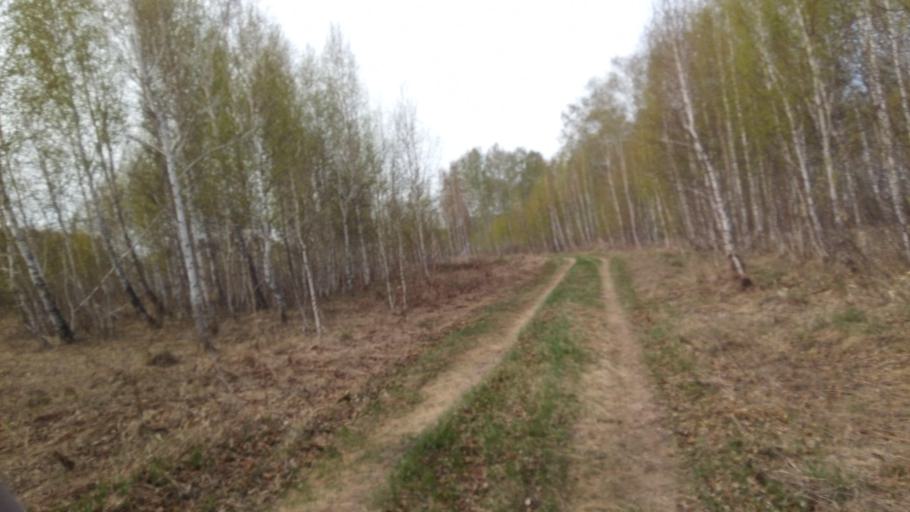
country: RU
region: Chelyabinsk
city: Timiryazevskiy
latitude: 55.0070
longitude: 60.8578
